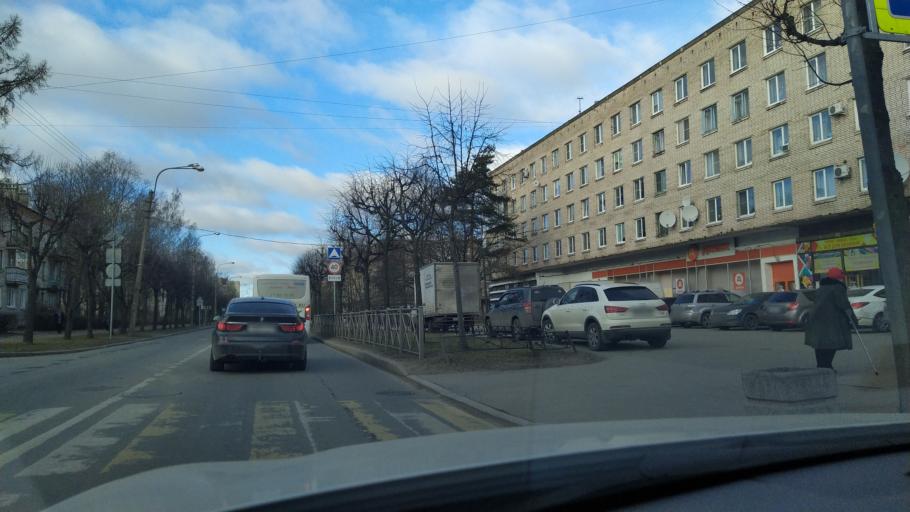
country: RU
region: St.-Petersburg
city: Pushkin
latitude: 59.7278
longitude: 30.4143
